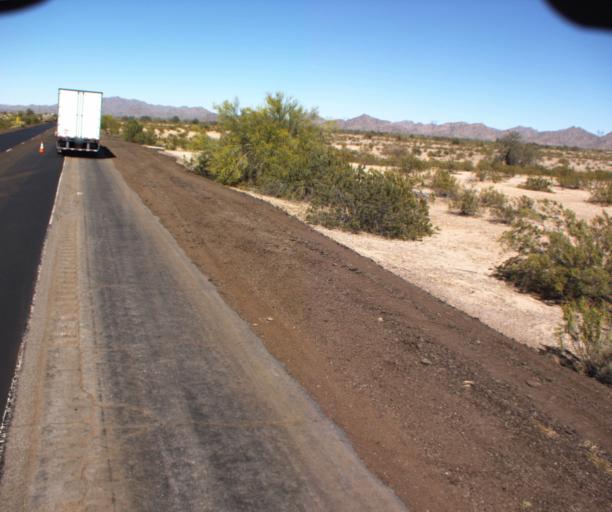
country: US
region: Arizona
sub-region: Maricopa County
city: Gila Bend
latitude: 33.0346
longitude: -112.6464
